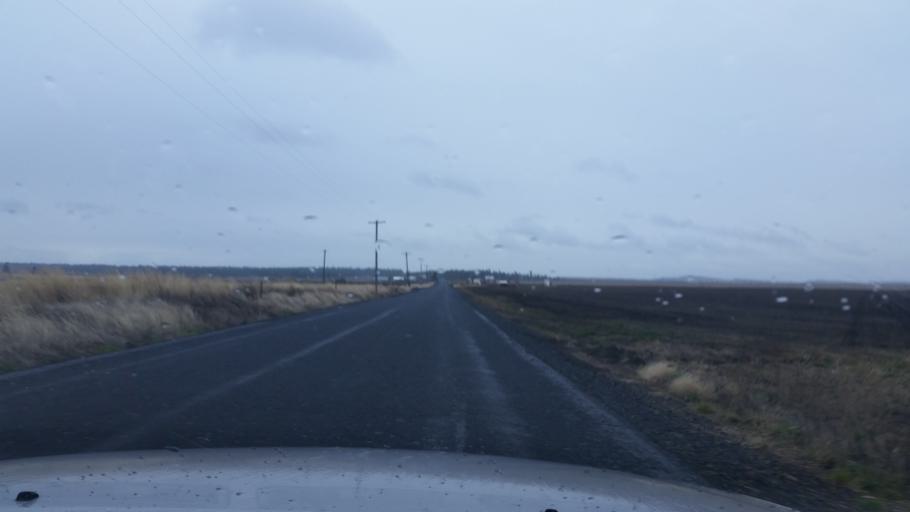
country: US
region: Washington
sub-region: Spokane County
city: Medical Lake
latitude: 47.6144
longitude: -117.7638
